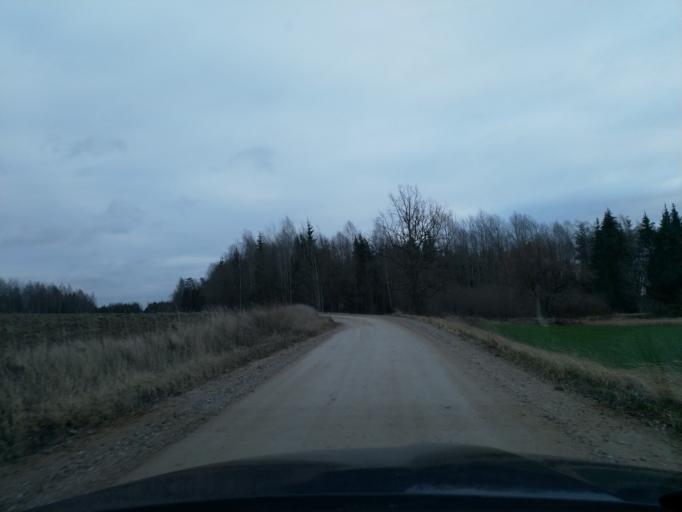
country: LV
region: Saldus Rajons
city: Saldus
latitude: 56.8925
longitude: 22.2852
